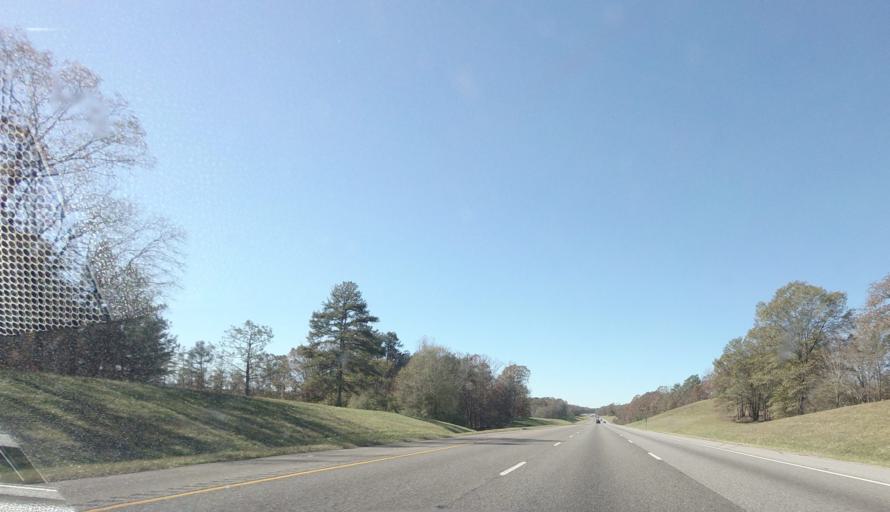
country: US
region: Alabama
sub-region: Calhoun County
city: Bynum
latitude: 33.5807
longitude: -85.9708
